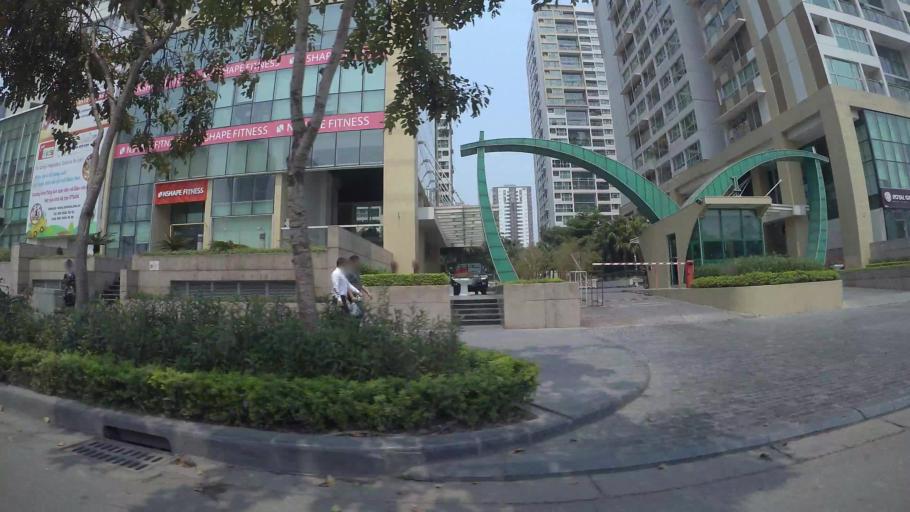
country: VN
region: Ha Noi
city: Thanh Xuan
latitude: 21.0050
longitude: 105.7983
